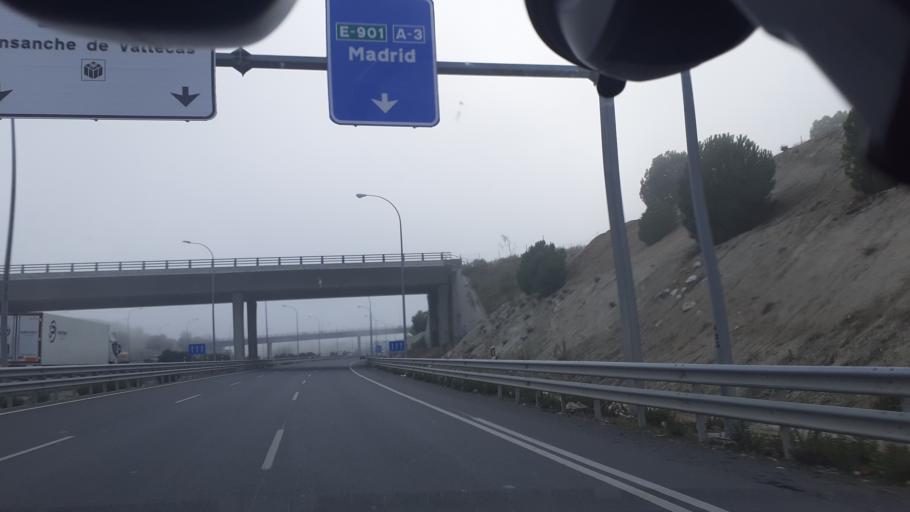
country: ES
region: Madrid
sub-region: Provincia de Madrid
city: Villa de Vallecas
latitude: 40.3787
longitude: -3.5913
